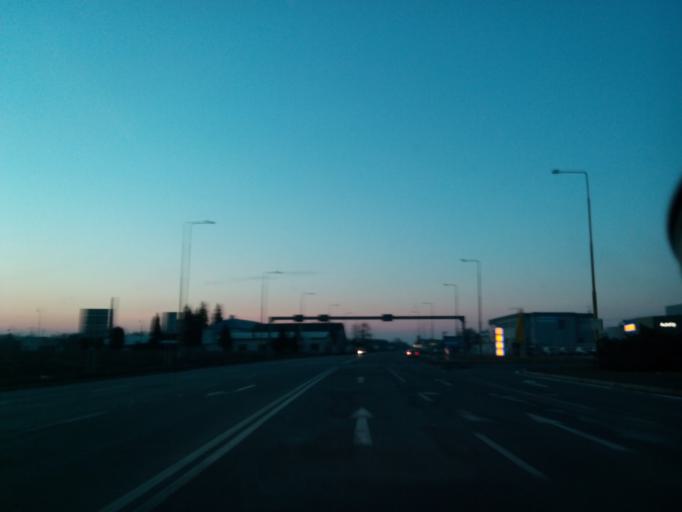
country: SK
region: Kosicky
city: Michalovce
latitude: 48.7529
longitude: 21.8992
